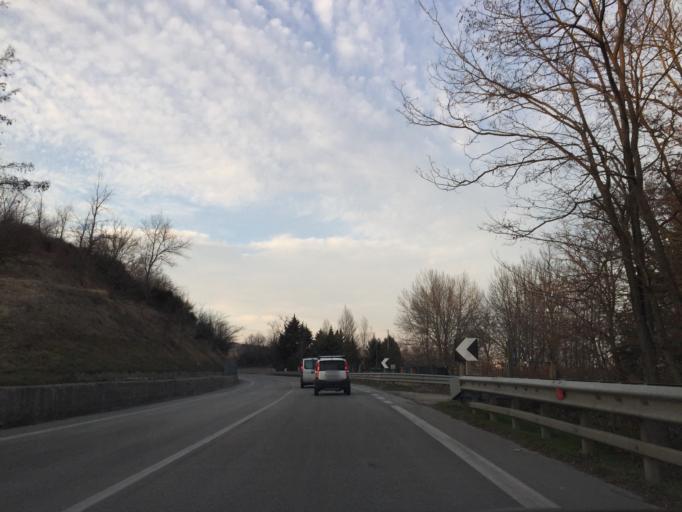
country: IT
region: Molise
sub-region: Provincia di Campobasso
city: Vinchiaturo
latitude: 41.5237
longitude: 14.6138
